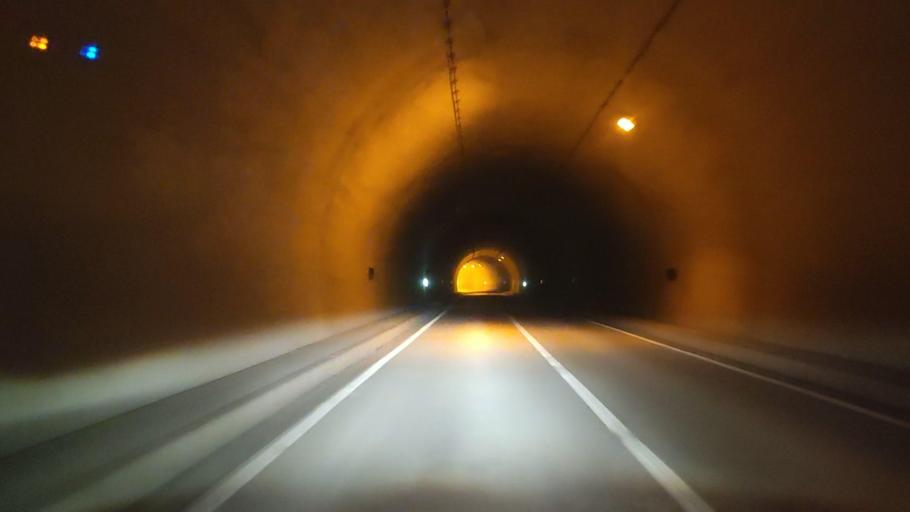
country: JP
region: Kumamoto
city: Matsubase
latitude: 32.5053
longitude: 130.9175
